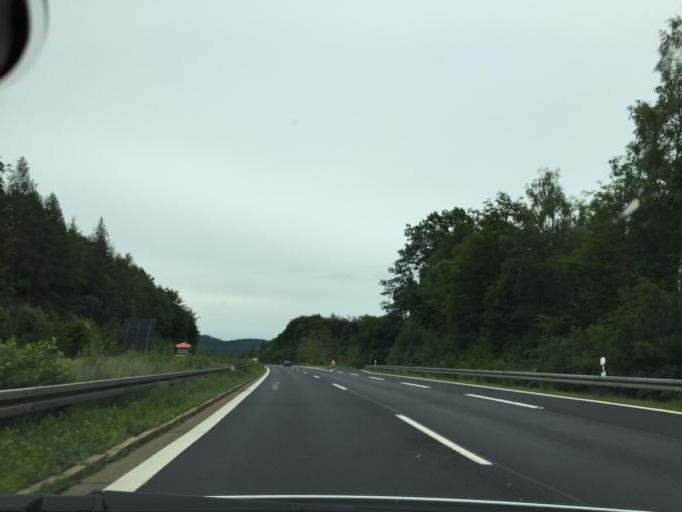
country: DE
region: Bavaria
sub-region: Regierungsbezirk Unterfranken
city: Bad Bruckenau
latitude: 50.3311
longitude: 9.7772
